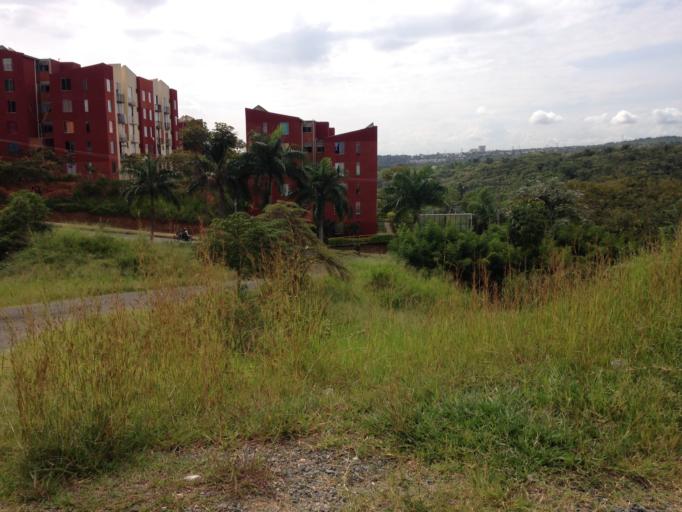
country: CO
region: Valle del Cauca
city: Cali
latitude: 3.3717
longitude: -76.5576
